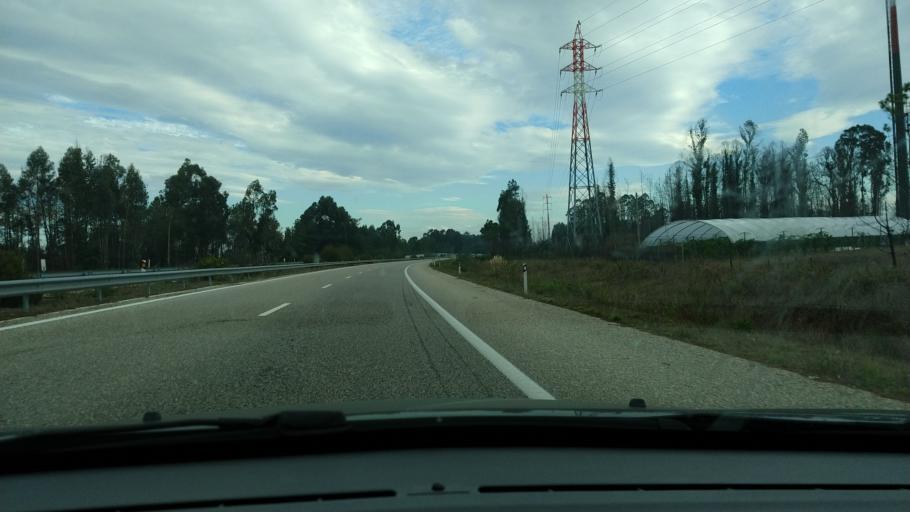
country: PT
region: Coimbra
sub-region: Mira
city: Mira
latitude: 40.4764
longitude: -8.6887
